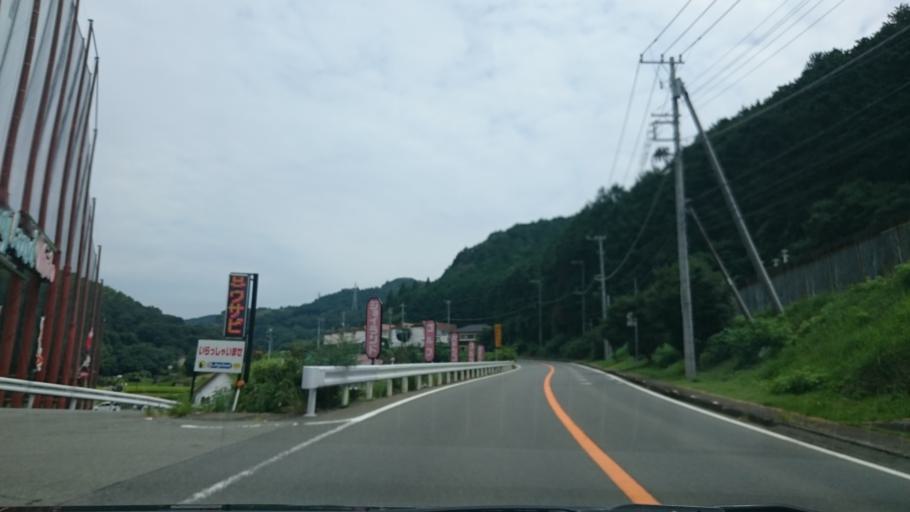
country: JP
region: Shizuoka
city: Mishima
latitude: 35.0057
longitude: 138.9622
